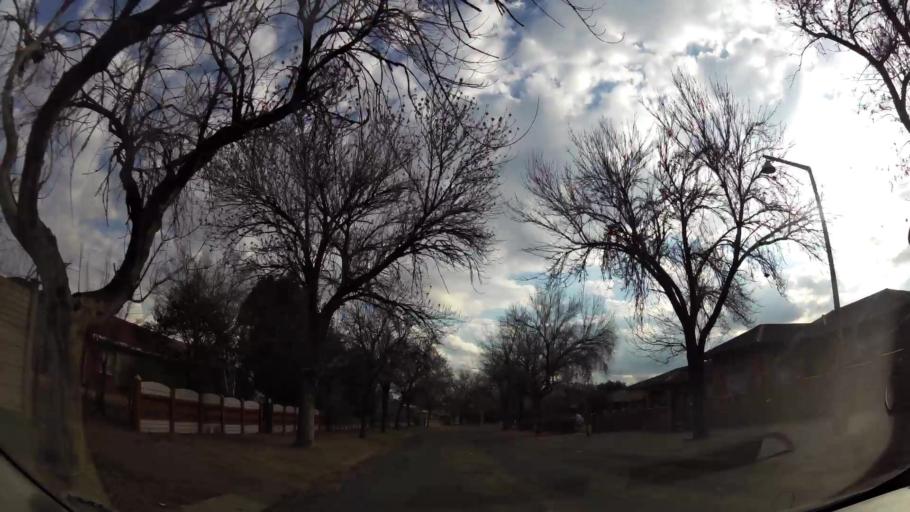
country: ZA
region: Orange Free State
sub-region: Fezile Dabi District Municipality
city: Sasolburg
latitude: -26.8251
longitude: 27.8267
